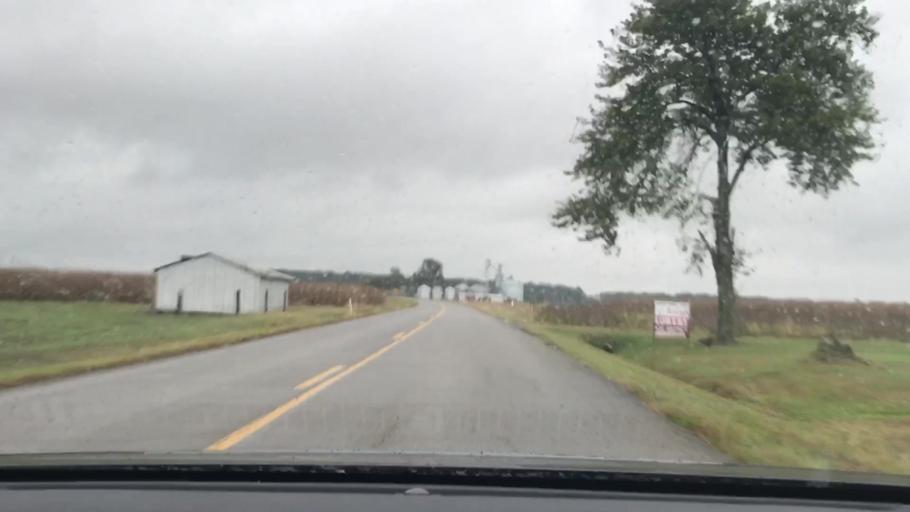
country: US
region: Kentucky
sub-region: McLean County
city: Calhoun
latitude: 37.5265
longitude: -87.3394
